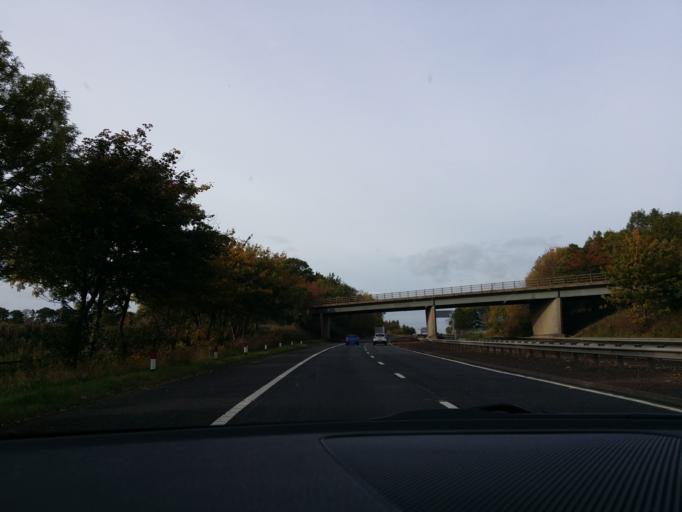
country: GB
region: Scotland
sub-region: Edinburgh
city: Kirkliston
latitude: 55.9607
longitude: -3.4413
